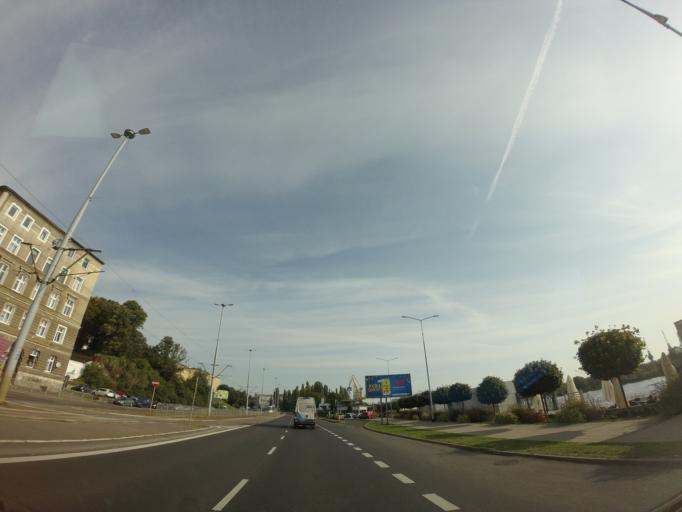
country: PL
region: West Pomeranian Voivodeship
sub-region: Szczecin
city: Szczecin
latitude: 53.4322
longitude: 14.5707
